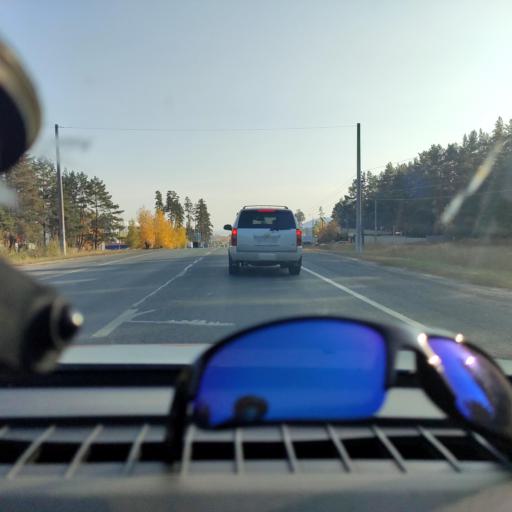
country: RU
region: Samara
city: Volzhskiy
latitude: 53.4404
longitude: 50.1239
